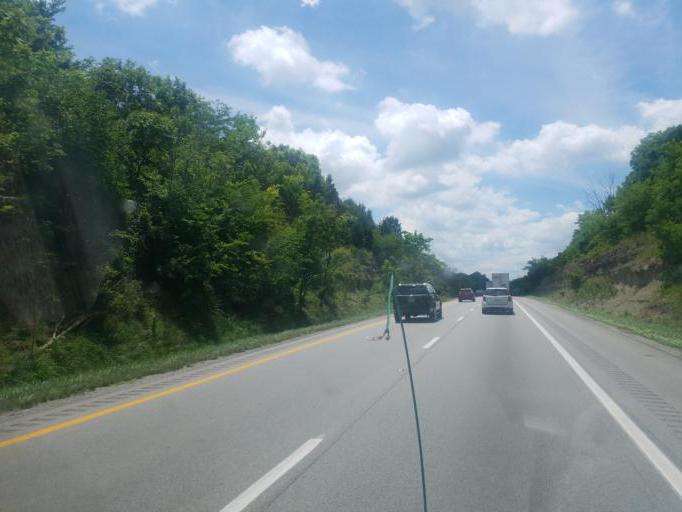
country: US
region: Kentucky
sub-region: Henry County
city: New Castle
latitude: 38.4726
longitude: -85.2770
